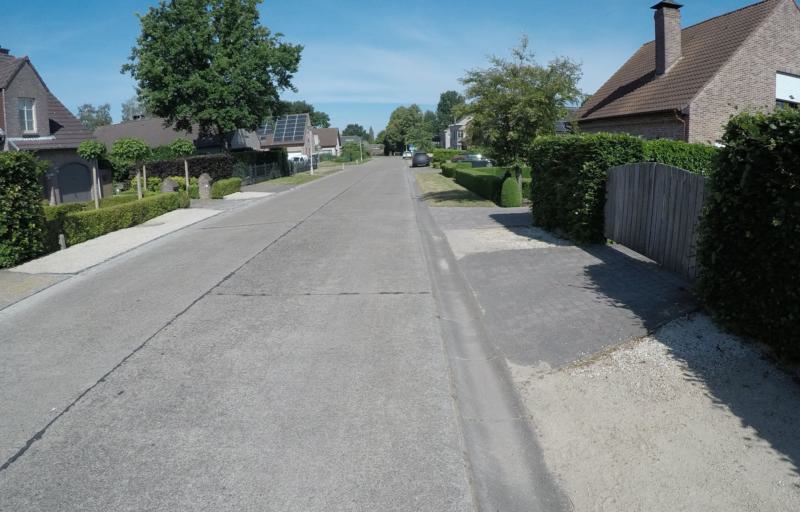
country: BE
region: Flanders
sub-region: Provincie Antwerpen
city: Wuustwezel
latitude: 51.3615
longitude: 4.5512
